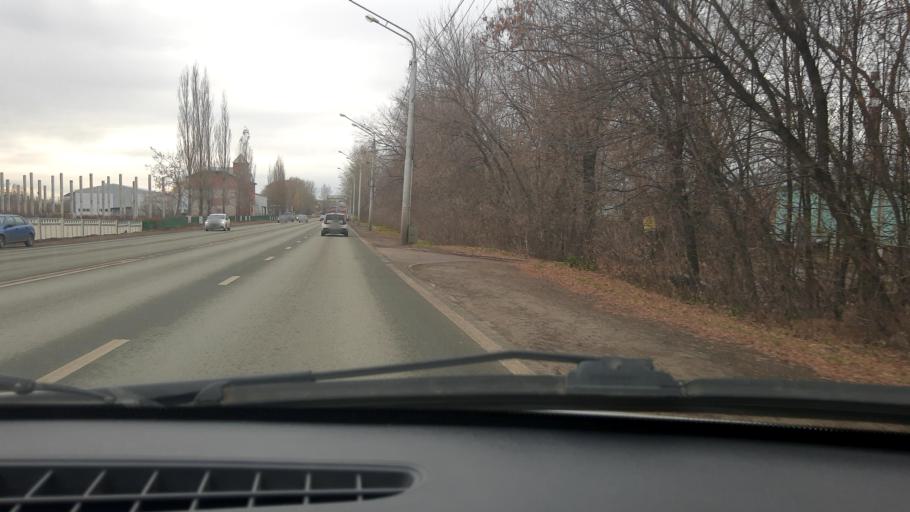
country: RU
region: Bashkortostan
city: Avdon
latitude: 54.6886
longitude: 55.8165
